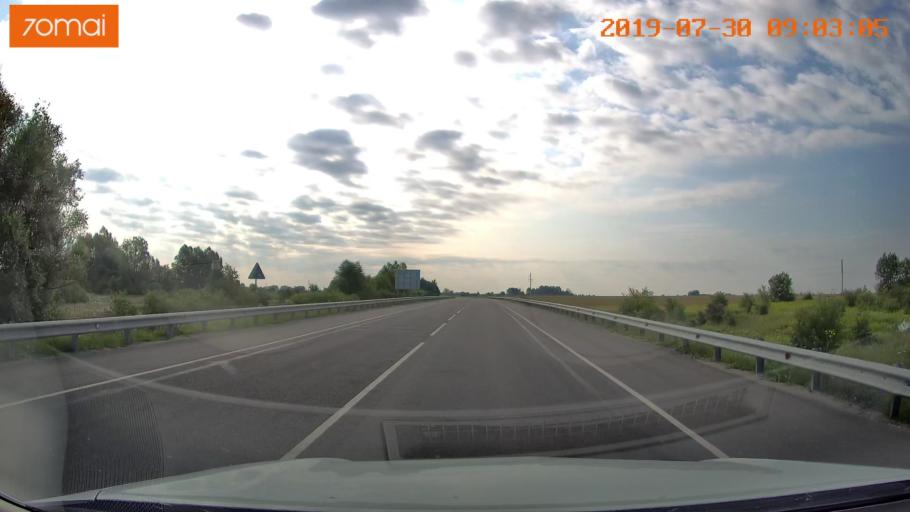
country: RU
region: Kaliningrad
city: Gusev
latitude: 54.6109
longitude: 22.2450
